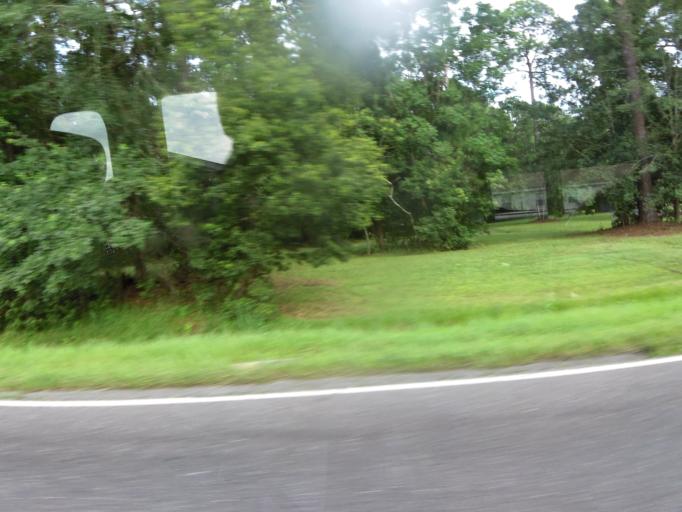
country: US
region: Florida
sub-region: Duval County
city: Jacksonville
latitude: 30.3592
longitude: -81.7515
